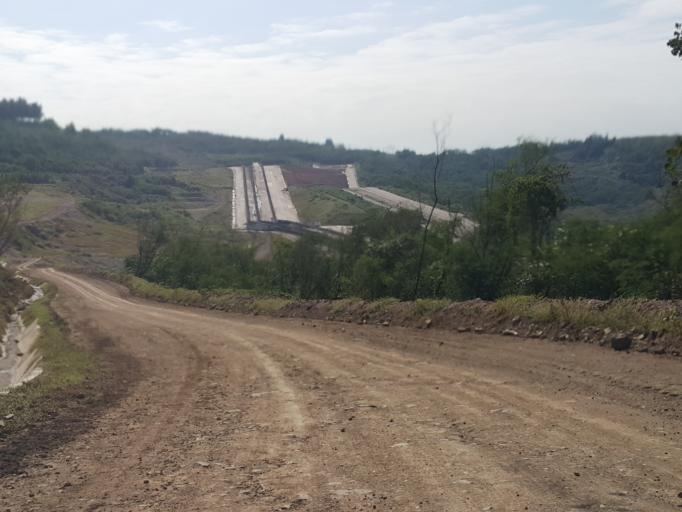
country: TH
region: Lampang
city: Mae Mo
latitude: 18.3264
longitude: 99.7374
